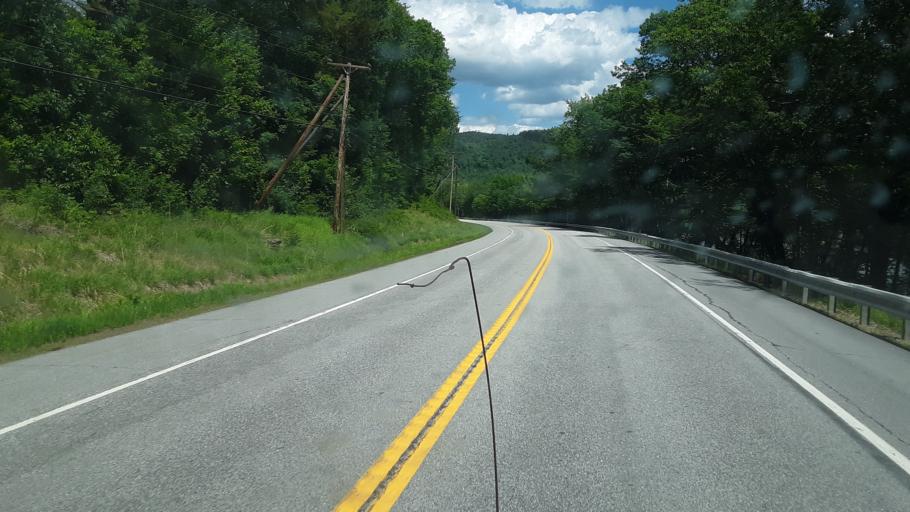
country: US
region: Maine
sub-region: Oxford County
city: Rumford
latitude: 44.5039
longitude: -70.6272
